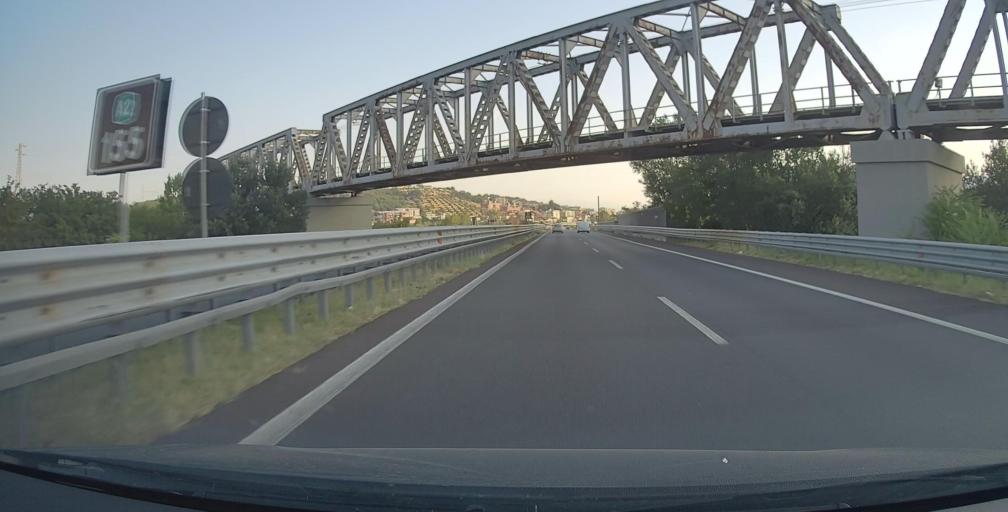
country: IT
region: Calabria
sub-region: Provincia di Cosenza
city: Settimo
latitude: 39.3768
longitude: 16.2364
